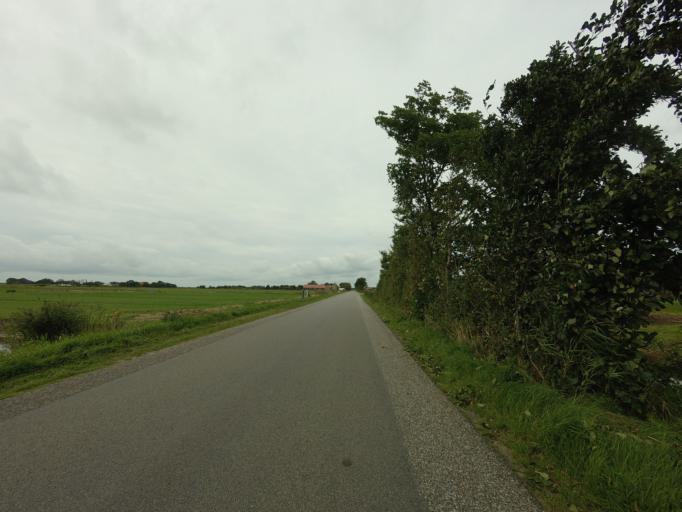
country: NL
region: Friesland
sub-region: Gemeente Ameland
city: Nes
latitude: 53.4397
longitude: 5.7157
